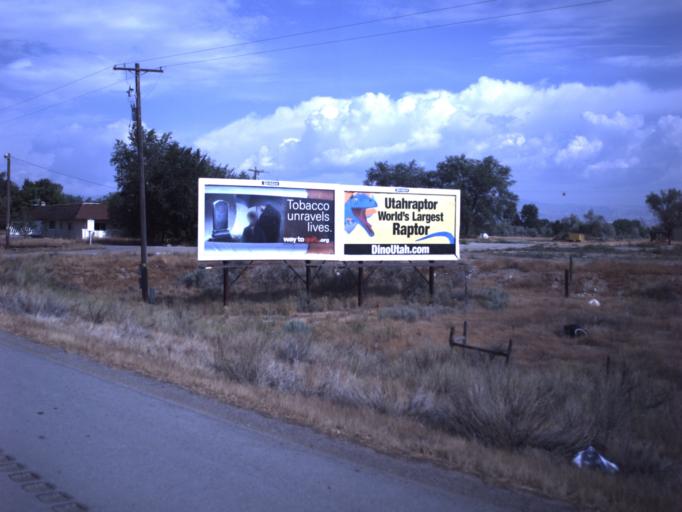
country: US
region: Utah
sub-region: Uintah County
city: Naples
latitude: 40.4081
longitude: -109.4846
